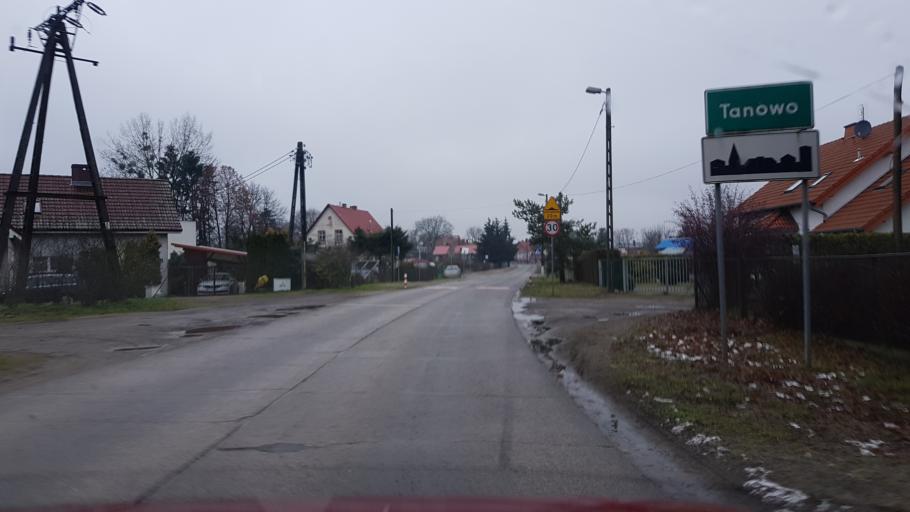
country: PL
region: West Pomeranian Voivodeship
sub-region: Powiat policki
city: Dobra
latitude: 53.5403
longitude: 14.4690
